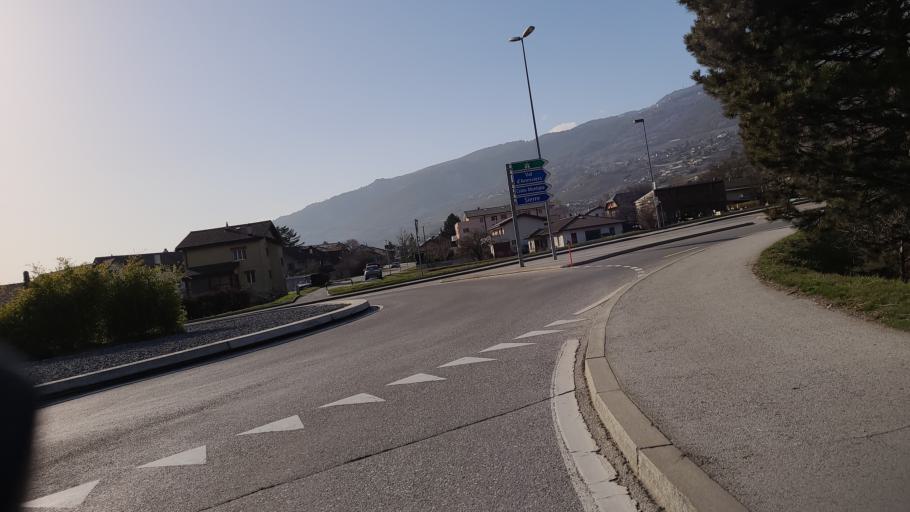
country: CH
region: Valais
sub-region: Sierre District
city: Veyras
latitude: 46.2969
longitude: 7.5503
